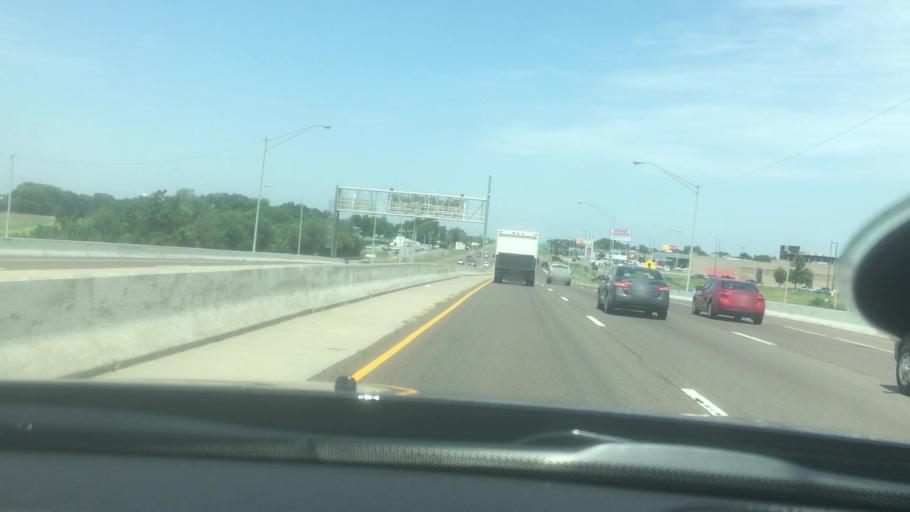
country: US
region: Oklahoma
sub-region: Oklahoma County
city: Del City
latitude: 35.4456
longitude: -97.4242
